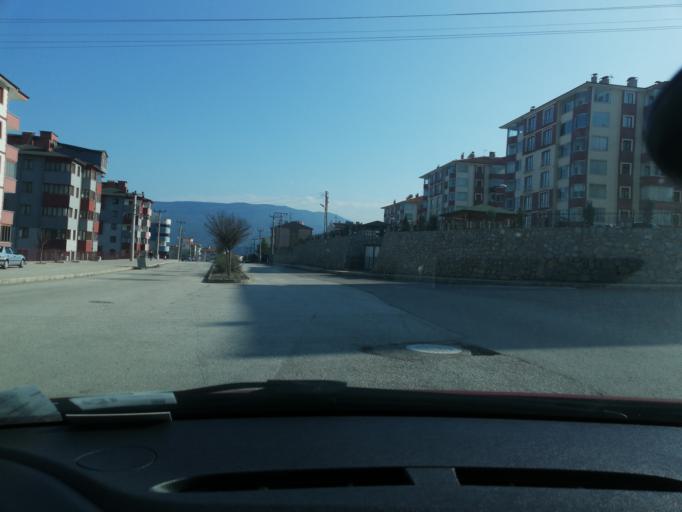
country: TR
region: Karabuk
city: Safranbolu
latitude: 41.2359
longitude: 32.6652
